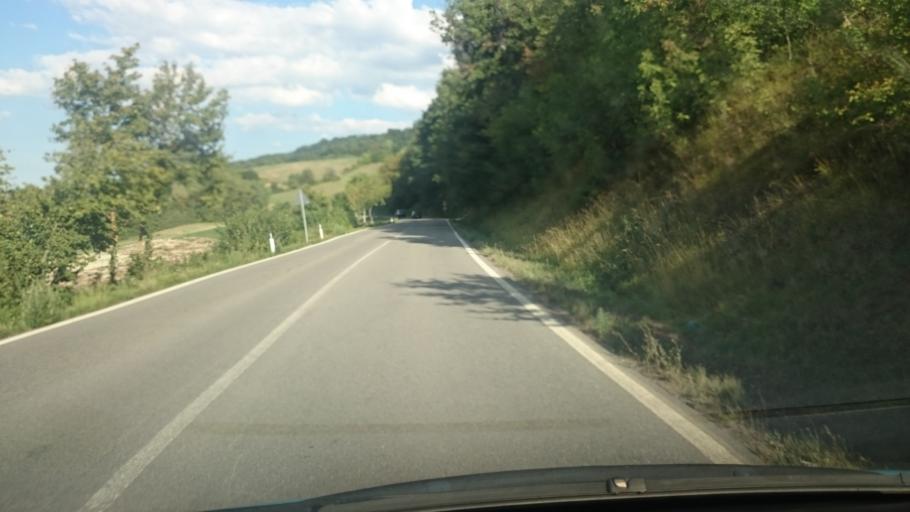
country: IT
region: Emilia-Romagna
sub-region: Provincia di Reggio Emilia
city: Carpineti
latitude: 44.4051
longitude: 10.5038
